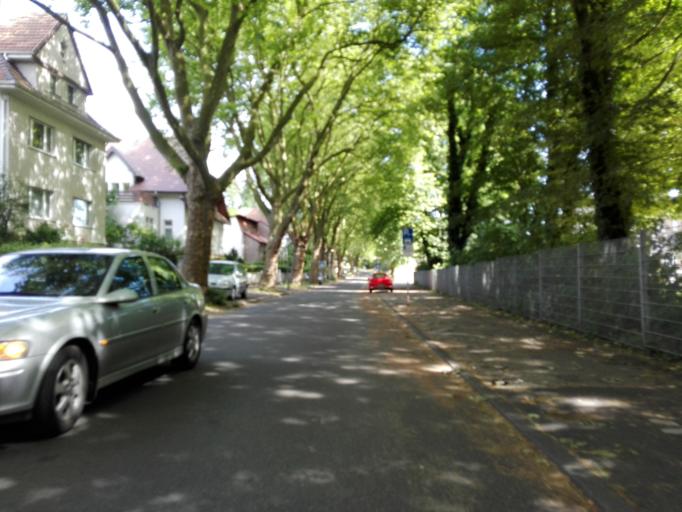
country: DE
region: North Rhine-Westphalia
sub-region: Regierungsbezirk Arnsberg
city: Unna
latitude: 51.5300
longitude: 7.6888
